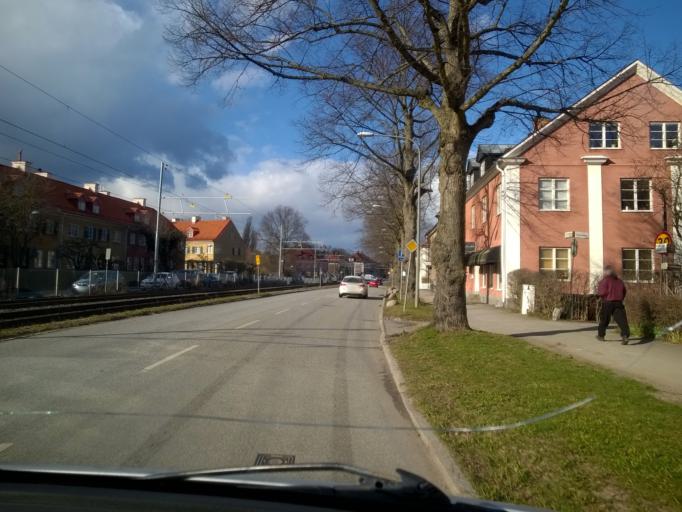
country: SE
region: Stockholm
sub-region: Sundbybergs Kommun
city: Sundbyberg
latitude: 59.3275
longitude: 17.9737
